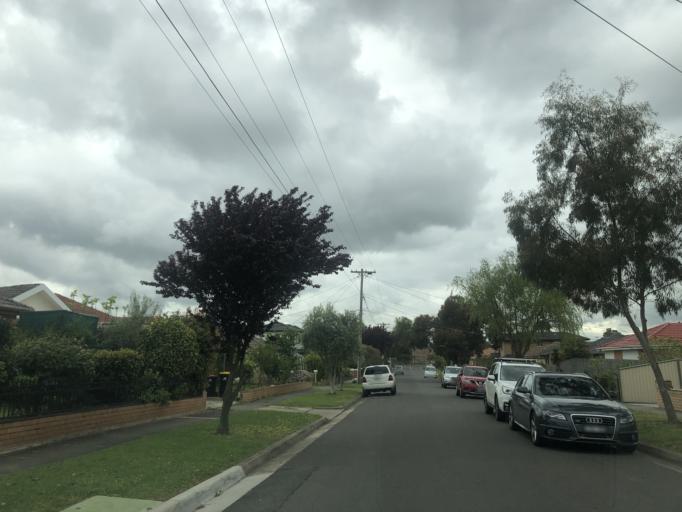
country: AU
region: Victoria
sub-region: Greater Dandenong
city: Dandenong North
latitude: -37.9718
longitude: 145.2149
